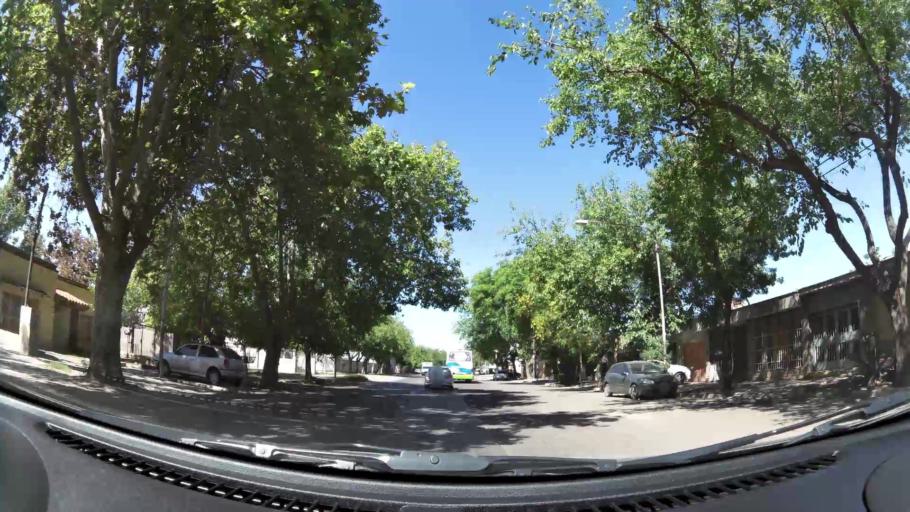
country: AR
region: Mendoza
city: Villa Nueva
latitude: -32.8950
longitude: -68.7829
